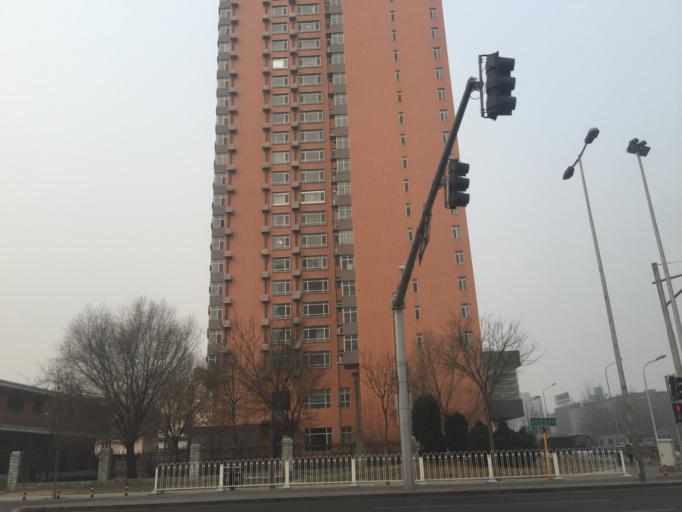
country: CN
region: Beijing
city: Datun
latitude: 40.0002
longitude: 116.3806
